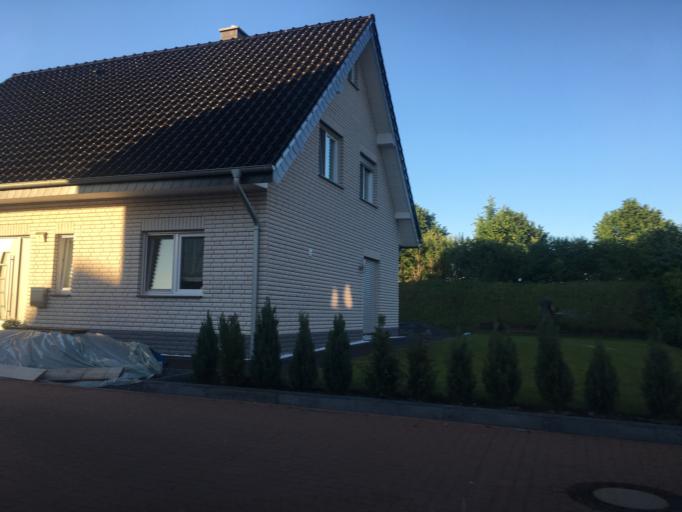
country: DE
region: North Rhine-Westphalia
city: Ludinghausen
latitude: 51.7622
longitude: 7.4618
